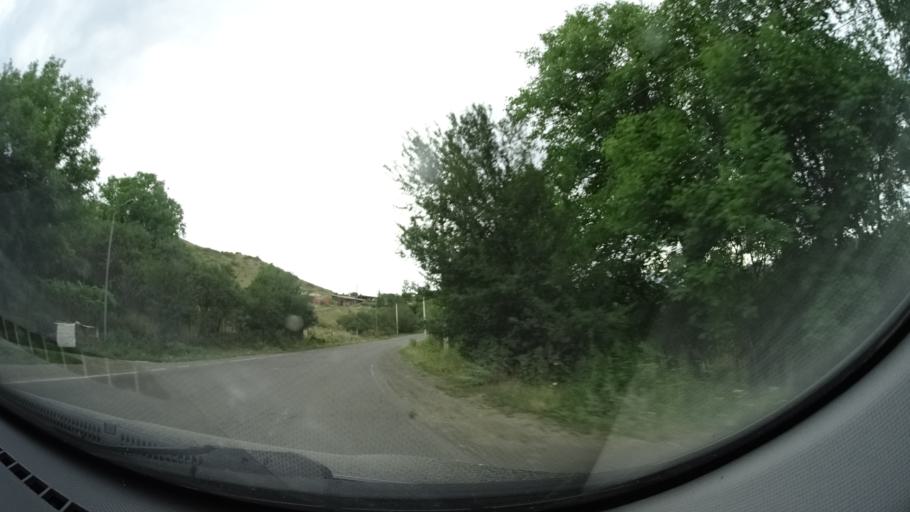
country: GE
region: Samtskhe-Javakheti
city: Akhaltsikhe
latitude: 41.6312
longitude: 43.0452
